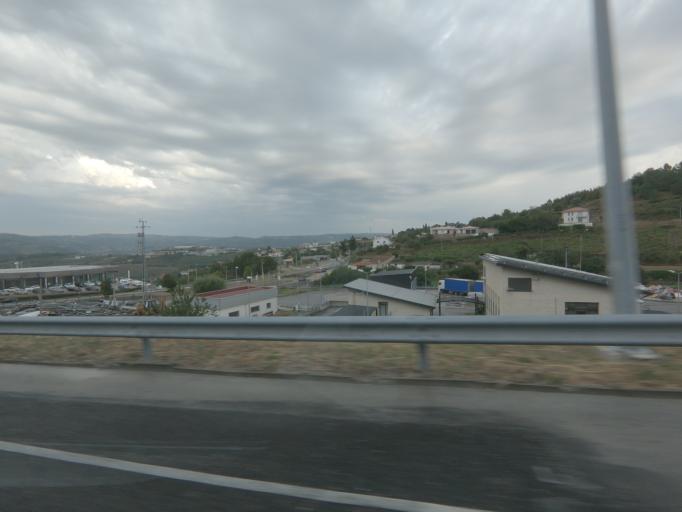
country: PT
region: Viseu
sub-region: Lamego
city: Lamego
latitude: 41.0799
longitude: -7.8005
